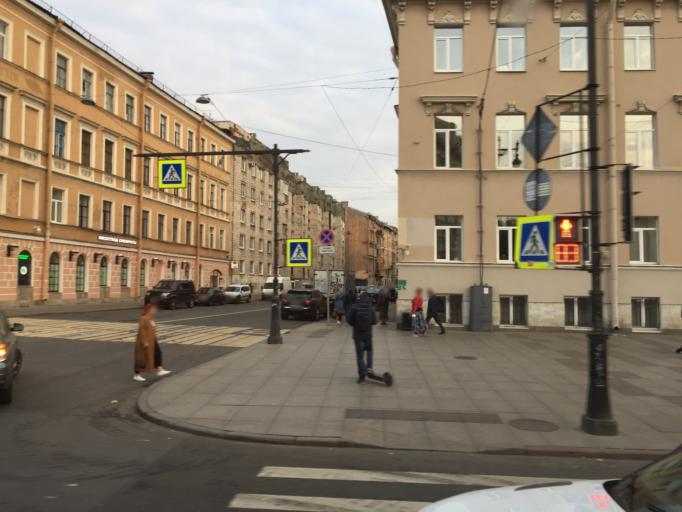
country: RU
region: St.-Petersburg
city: Saint Petersburg
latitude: 59.9171
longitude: 30.3196
